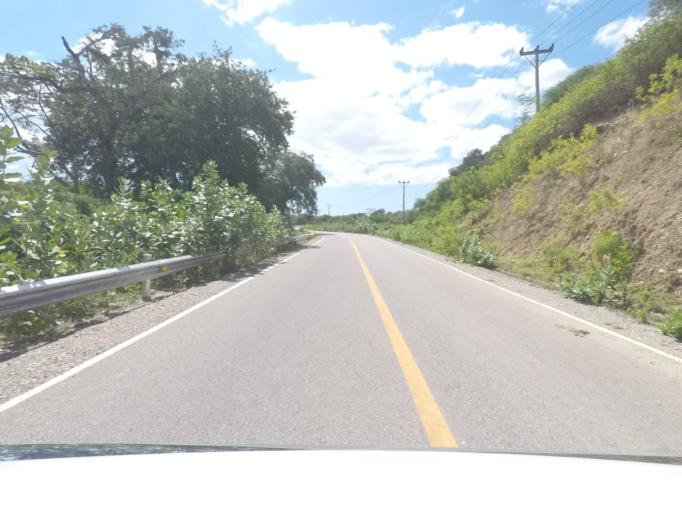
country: TL
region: Lautem
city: Lospalos
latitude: -8.3706
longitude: 126.8945
